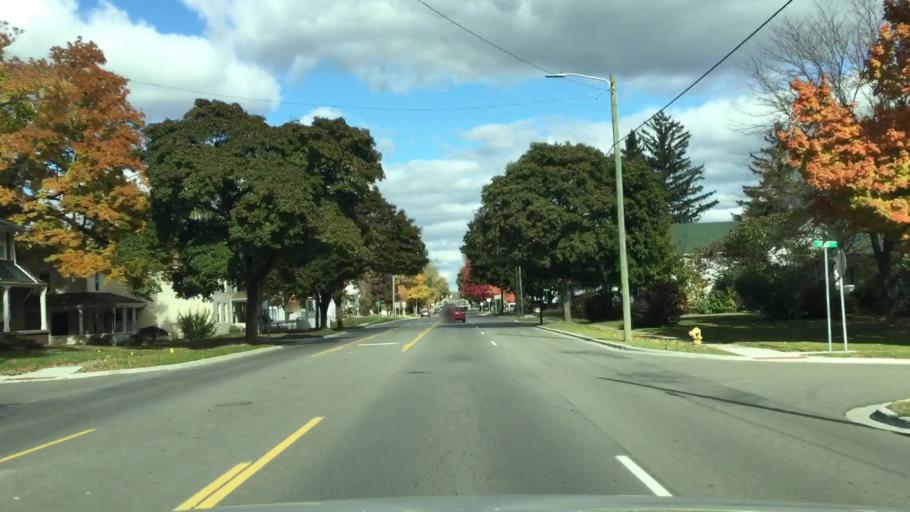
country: US
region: Michigan
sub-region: Lapeer County
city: Lapeer
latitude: 43.0531
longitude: -83.3188
